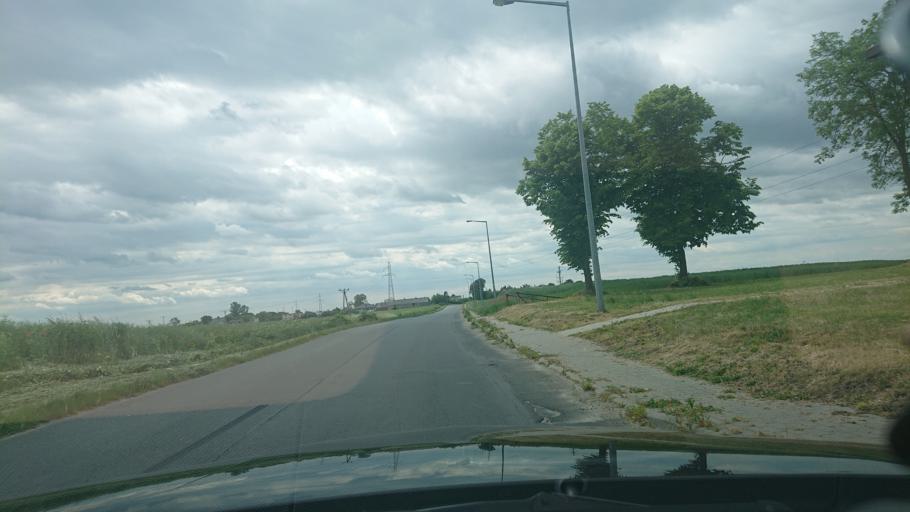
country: PL
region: Greater Poland Voivodeship
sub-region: Powiat gnieznienski
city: Gniezno
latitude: 52.5410
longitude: 17.5557
